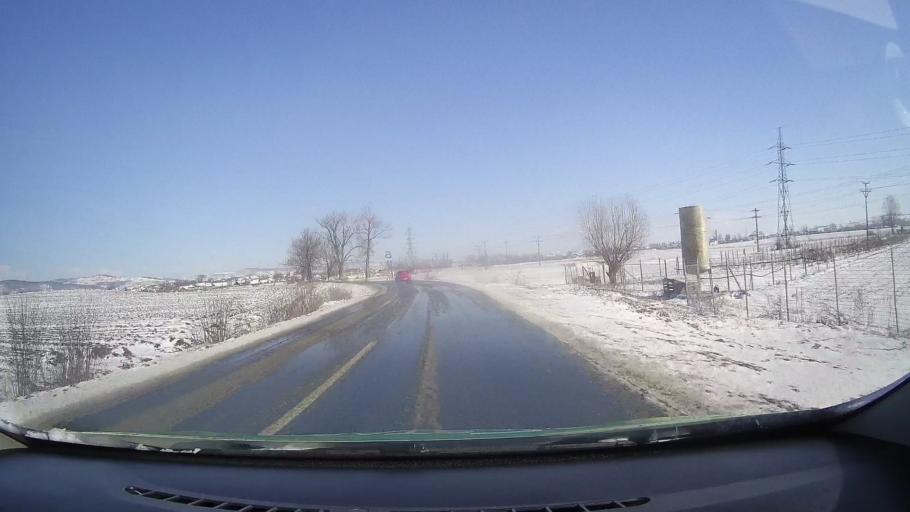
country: RO
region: Sibiu
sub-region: Comuna Avrig
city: Avrig
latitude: 45.7155
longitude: 24.3724
